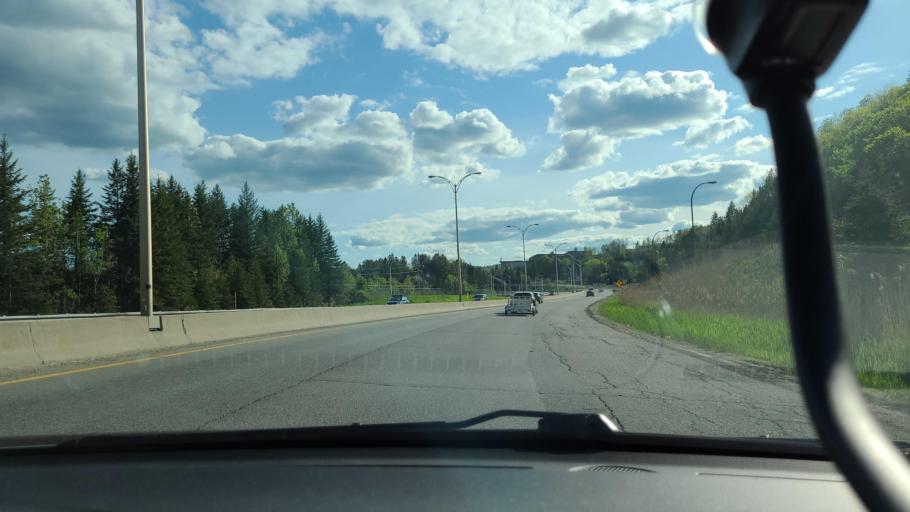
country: CA
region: Quebec
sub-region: Laurentides
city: Sainte-Adele
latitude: 45.9415
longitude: -74.1265
